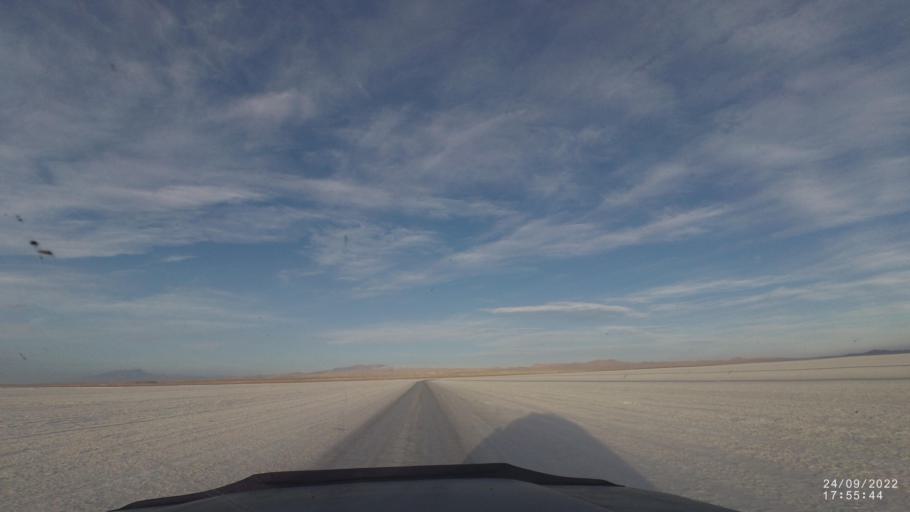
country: BO
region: Potosi
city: Colchani
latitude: -20.3266
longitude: -67.0259
